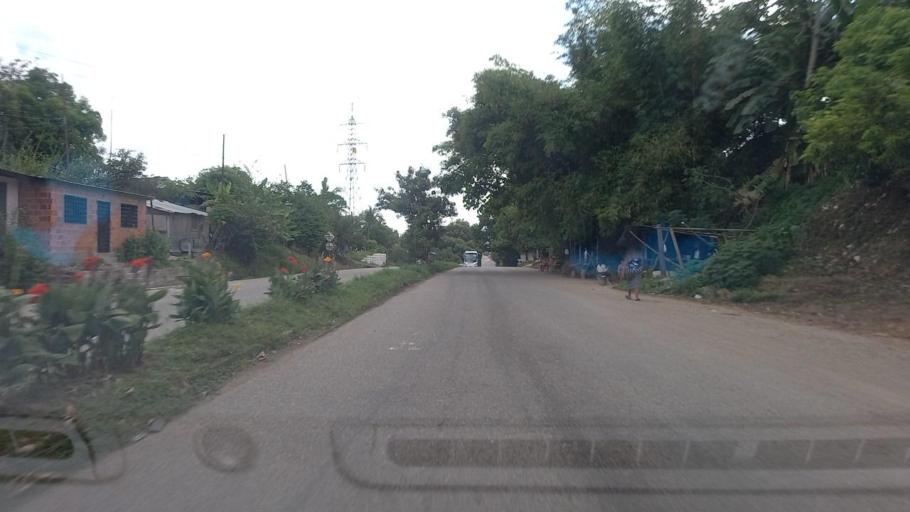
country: CO
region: Santander
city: Sabana de Torres
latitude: 7.1310
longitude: -73.5618
